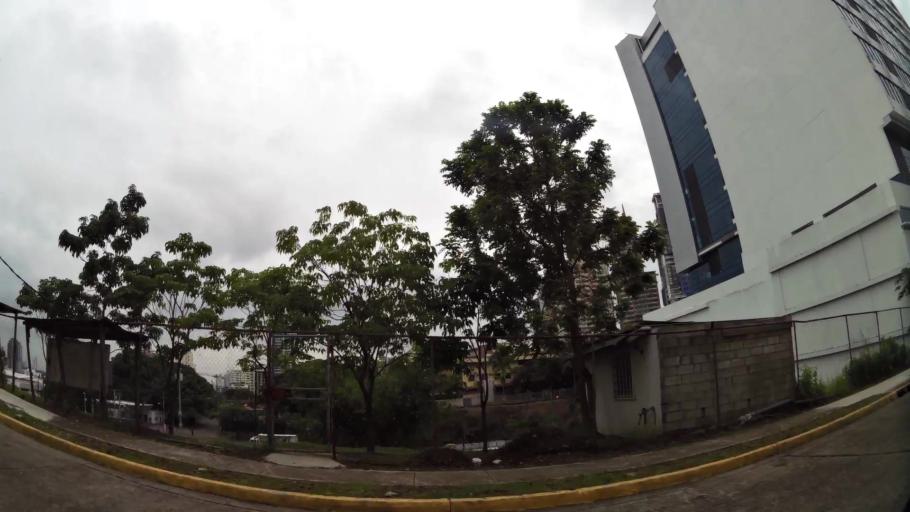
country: PA
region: Panama
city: Panama
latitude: 8.9925
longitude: -79.5311
